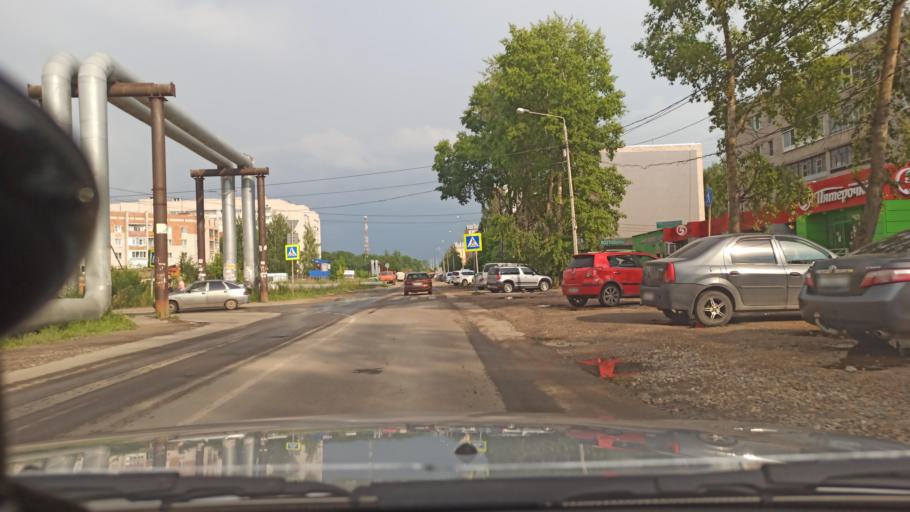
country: RU
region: Vologda
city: Vologda
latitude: 59.1878
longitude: 39.9066
